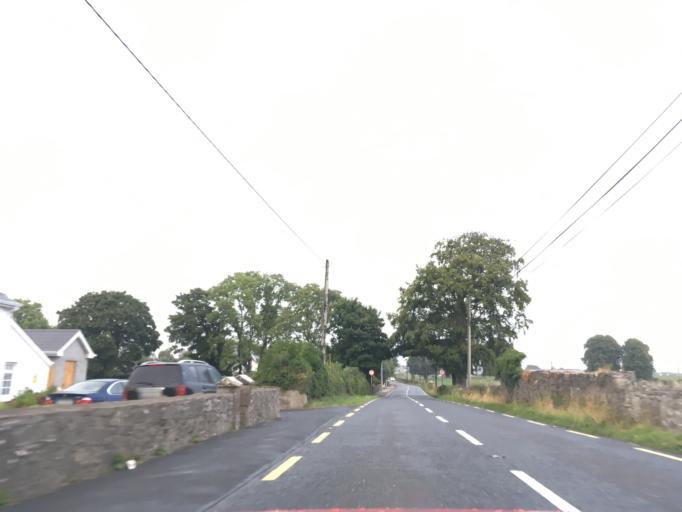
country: IE
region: Munster
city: Tipperary
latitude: 52.4921
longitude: -8.0302
